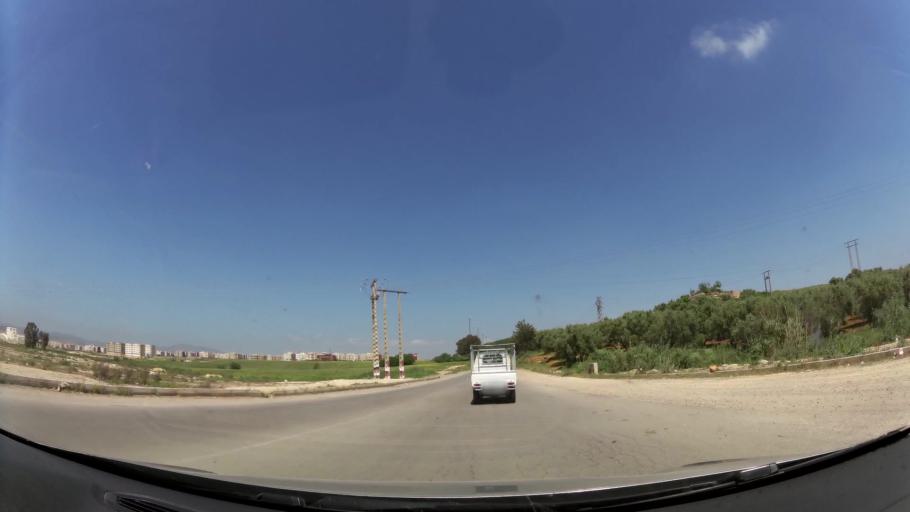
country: MA
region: Fes-Boulemane
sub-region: Fes
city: Fes
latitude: 34.0023
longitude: -5.0400
